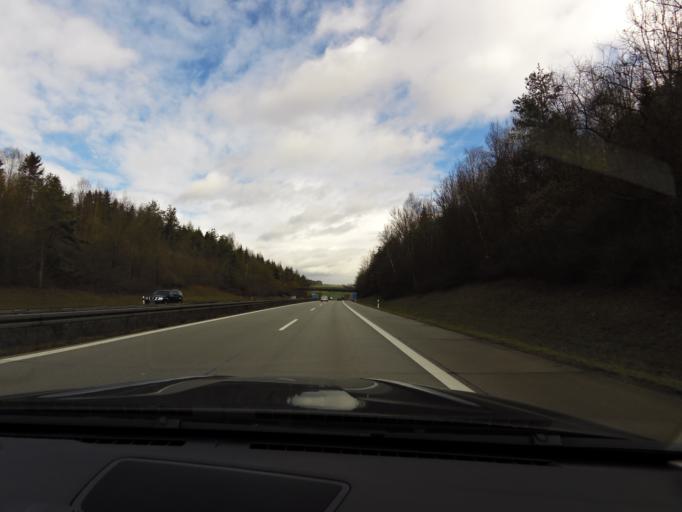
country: DE
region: Bavaria
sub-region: Lower Bavaria
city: Weihmichl
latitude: 48.5612
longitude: 12.0819
